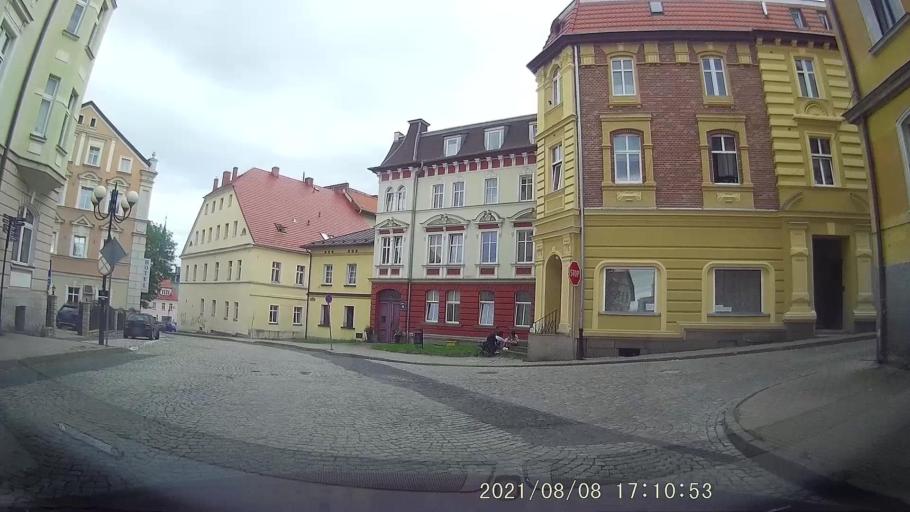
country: PL
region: Lower Silesian Voivodeship
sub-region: Powiat klodzki
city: Duszniki-Zdroj
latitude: 50.4047
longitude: 16.3885
